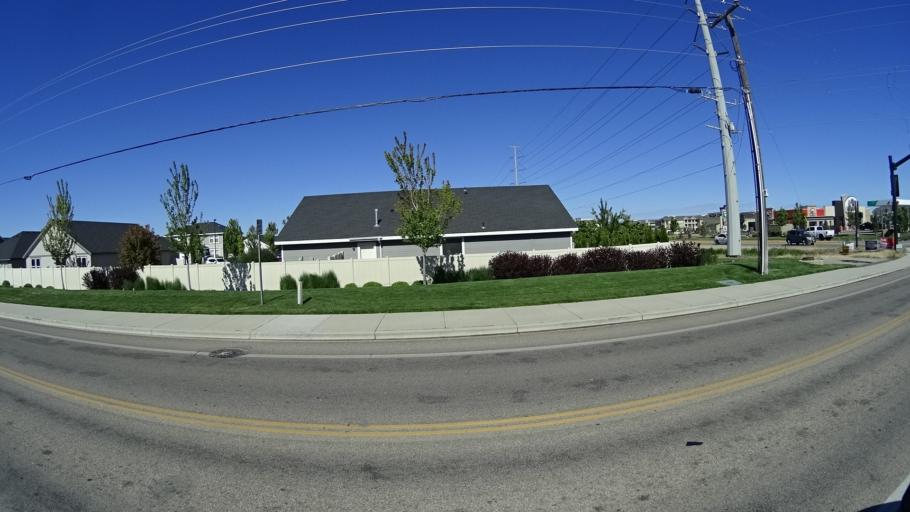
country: US
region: Idaho
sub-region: Ada County
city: Meridian
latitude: 43.6480
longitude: -116.3946
